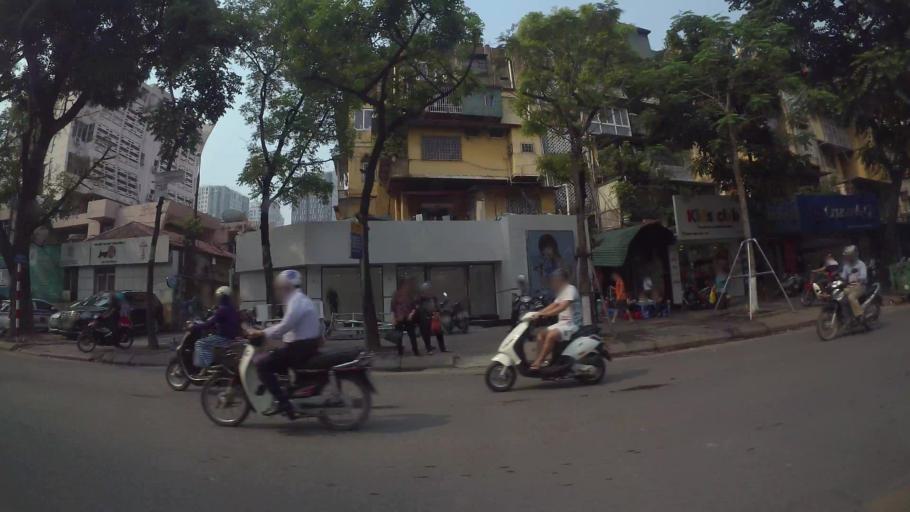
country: VN
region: Ha Noi
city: Dong Da
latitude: 21.0173
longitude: 105.8136
